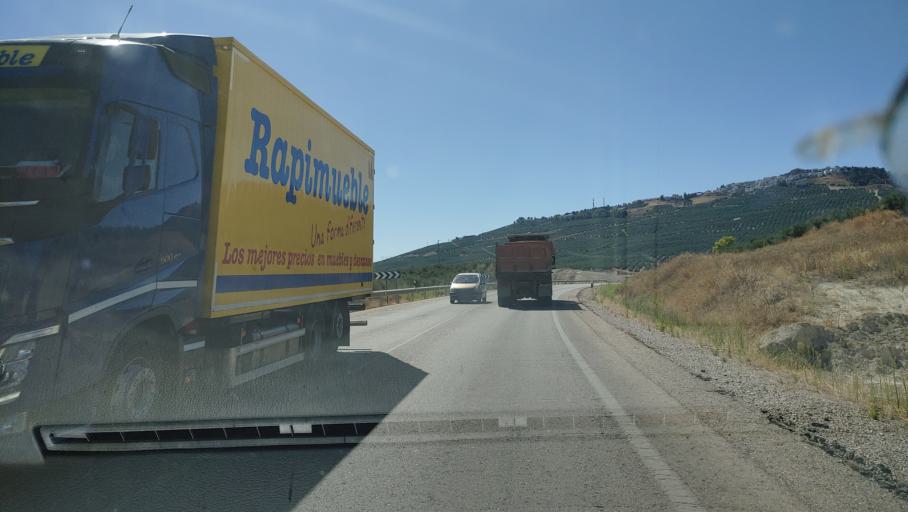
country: ES
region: Andalusia
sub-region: Provincia de Jaen
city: Villanueva del Arzobispo
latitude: 38.1550
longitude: -3.0062
